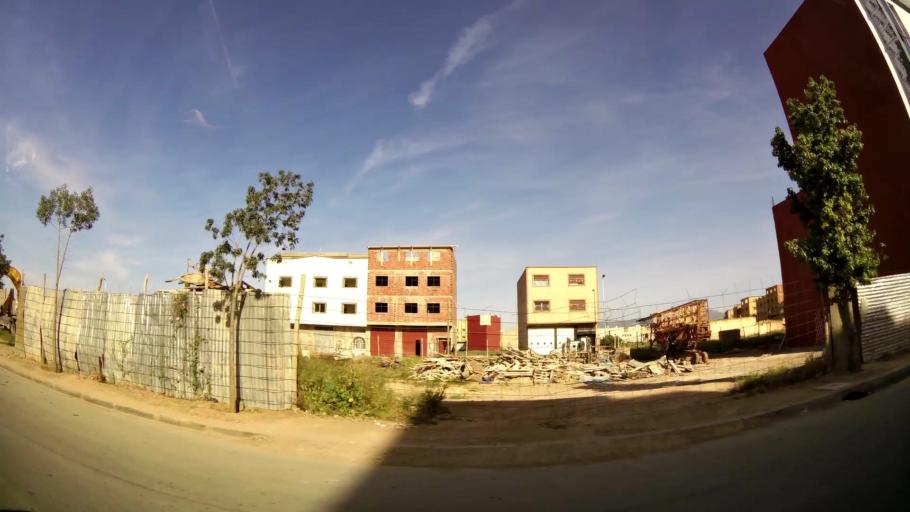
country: MA
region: Oriental
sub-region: Oujda-Angad
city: Oujda
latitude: 34.6701
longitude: -1.8943
